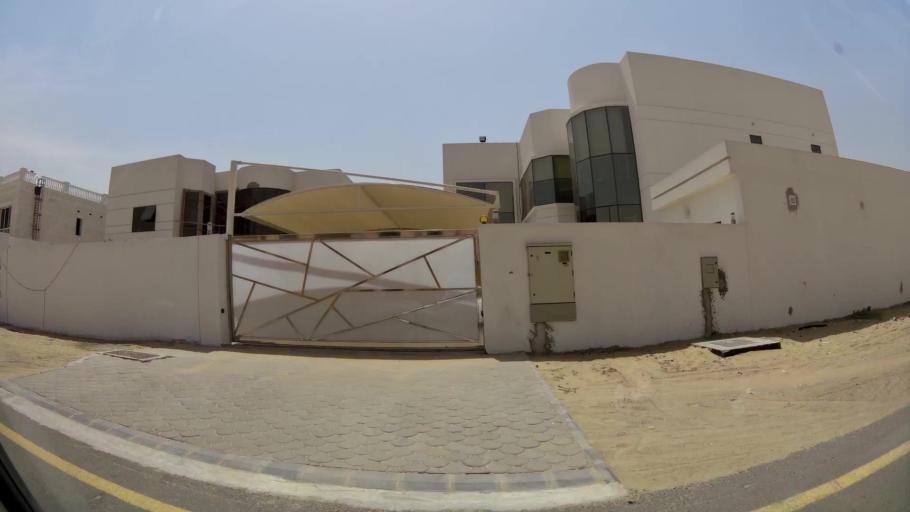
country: AE
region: Ash Shariqah
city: Sharjah
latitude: 25.2559
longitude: 55.4991
